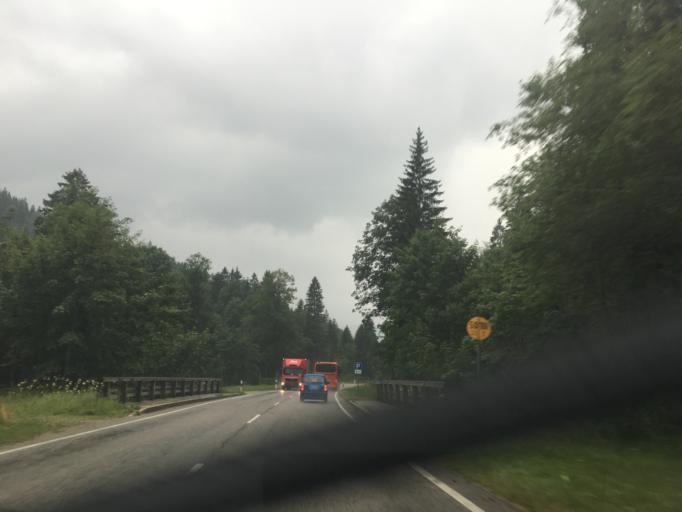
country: DE
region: Bavaria
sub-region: Upper Bavaria
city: Reit im Winkl
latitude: 47.6791
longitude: 12.4994
